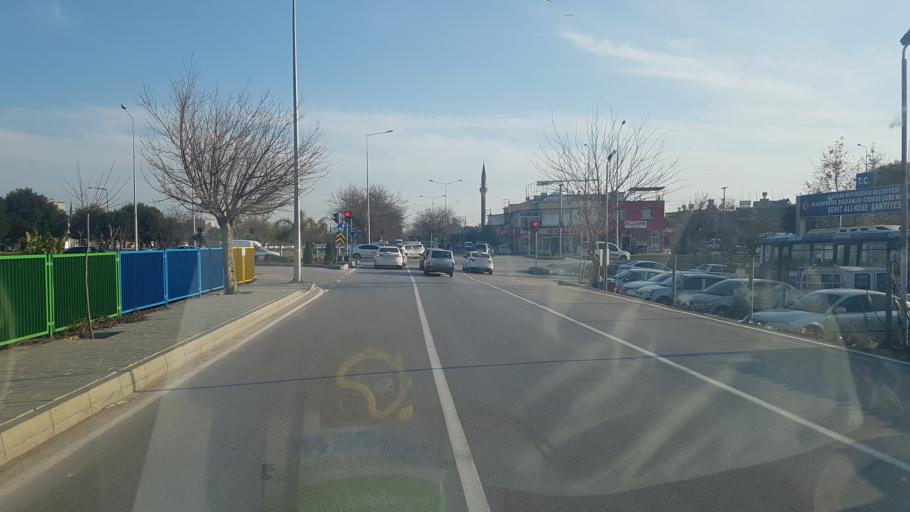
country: TR
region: Adana
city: Adana
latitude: 37.0082
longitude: 35.3533
